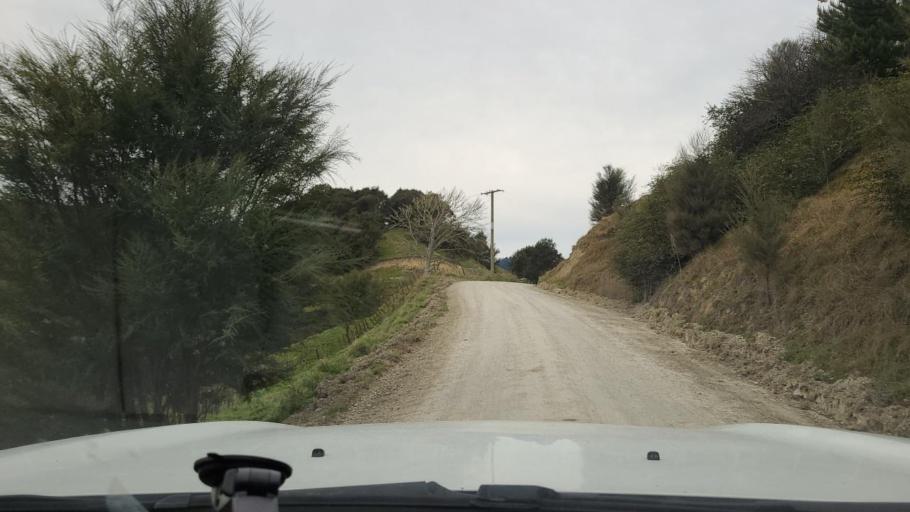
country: NZ
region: Gisborne
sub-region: Gisborne District
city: Gisborne
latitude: -38.5800
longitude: 178.0454
